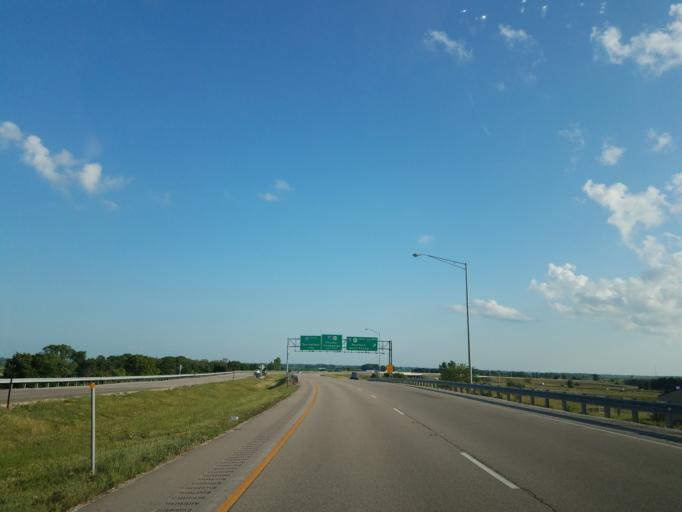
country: US
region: Illinois
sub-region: McLean County
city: Bloomington
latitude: 40.4471
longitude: -89.0164
